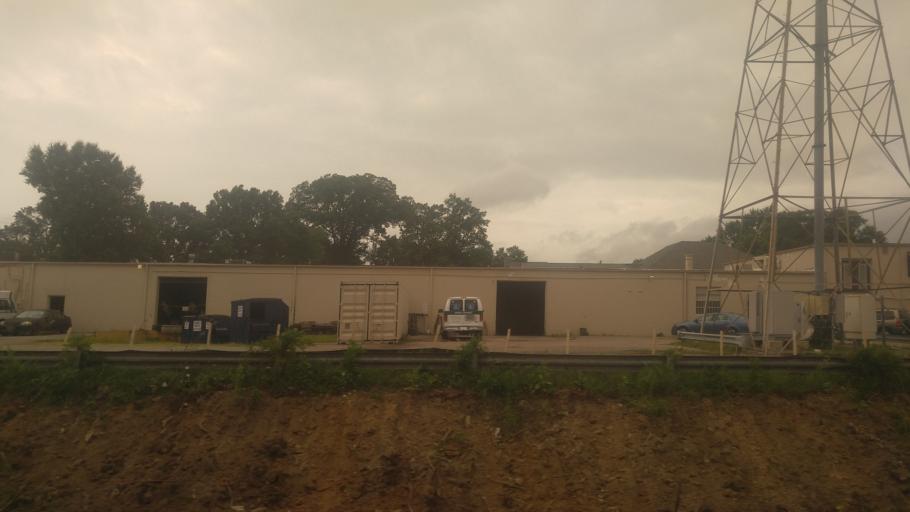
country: US
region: Virginia
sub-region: Henrico County
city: Dumbarton
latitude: 37.6047
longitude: -77.4904
